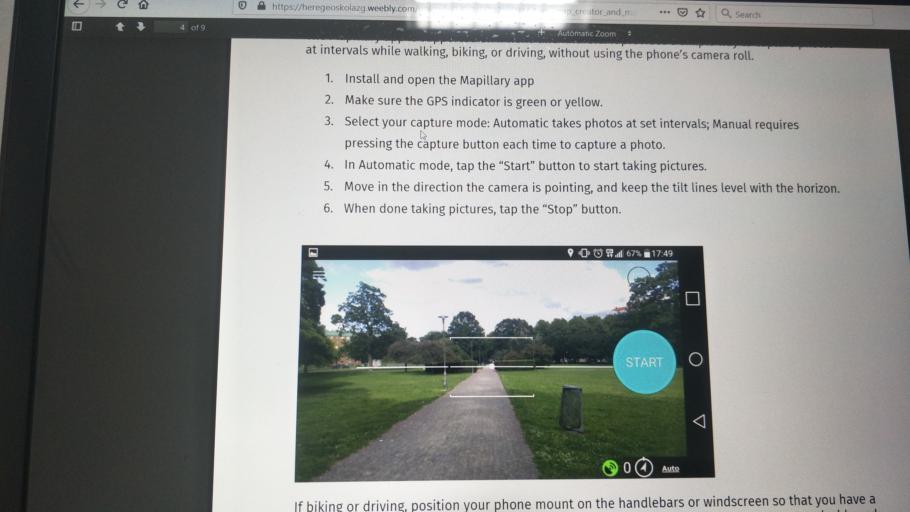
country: KH
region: Phnom Penh
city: Phnom Penh
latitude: 11.5736
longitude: 104.9214
